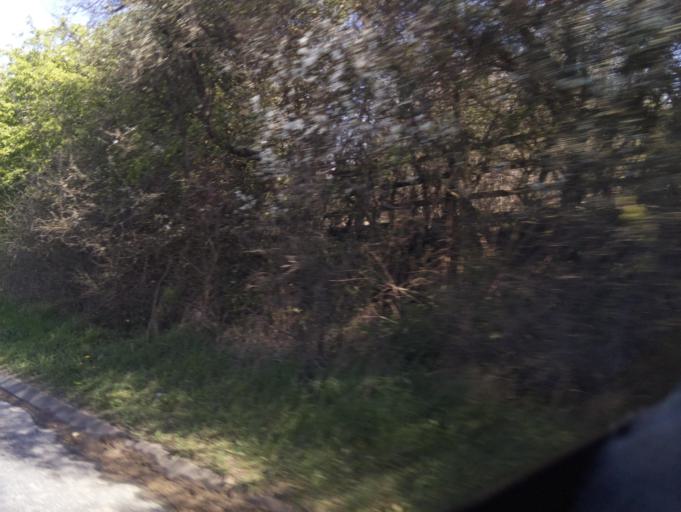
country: GB
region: England
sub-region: Wiltshire
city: Bradford-on-Avon
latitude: 51.3684
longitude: -2.2706
